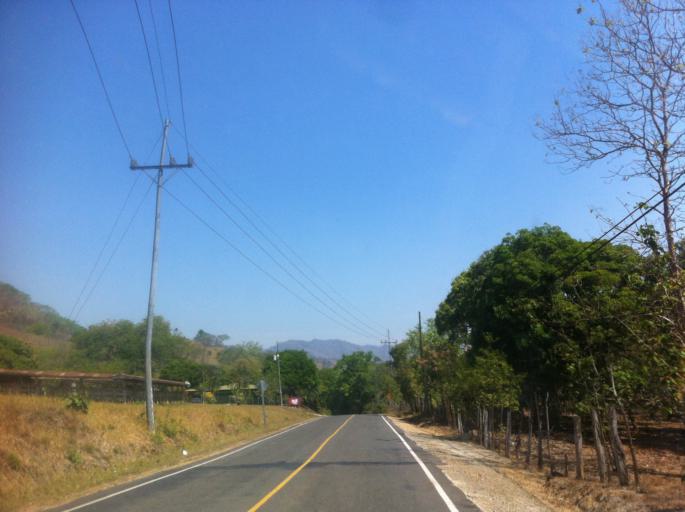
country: CR
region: Guanacaste
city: Hojancha
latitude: 10.0166
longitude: -85.5012
